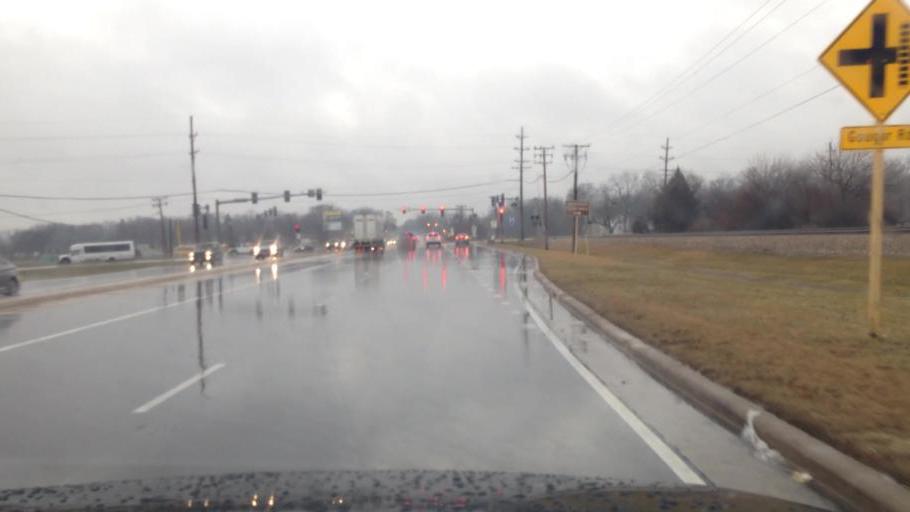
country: US
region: Illinois
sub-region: Will County
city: New Lenox
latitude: 41.5231
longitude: -88.0032
